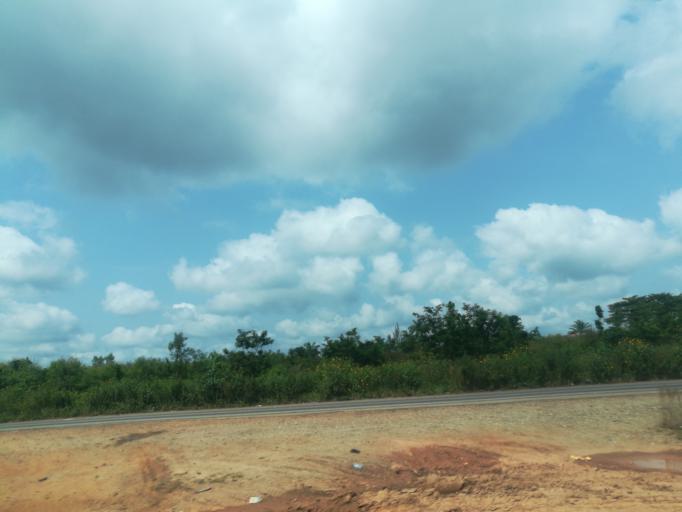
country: NG
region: Oyo
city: Moniya
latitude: 7.5826
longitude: 3.9153
